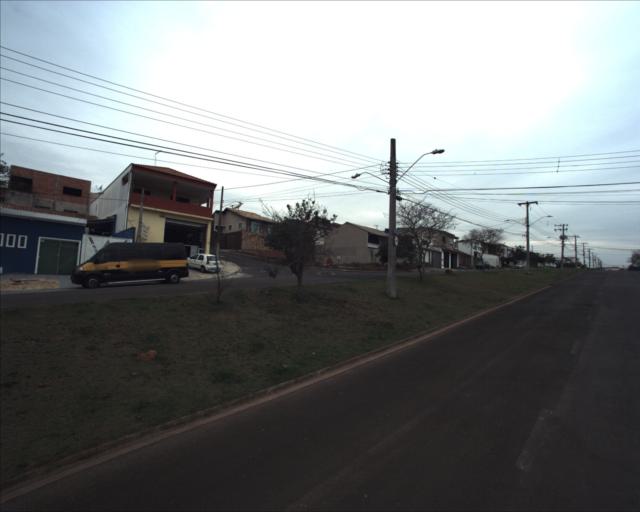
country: BR
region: Sao Paulo
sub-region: Sorocaba
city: Sorocaba
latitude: -23.4912
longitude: -47.5161
